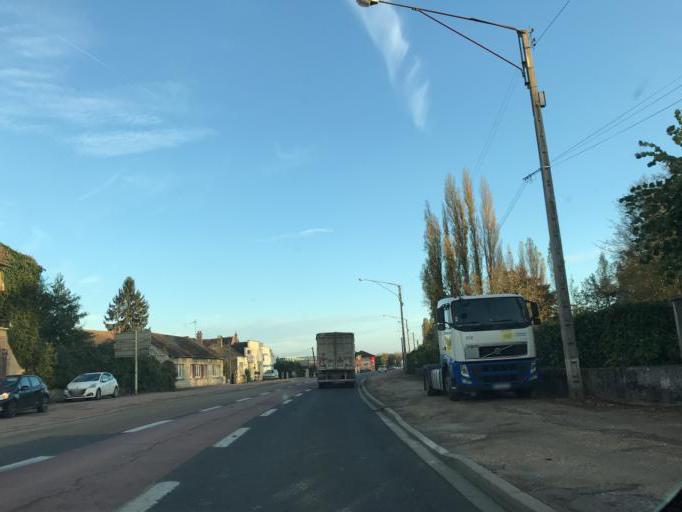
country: FR
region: Bourgogne
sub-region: Departement de l'Yonne
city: Pont-sur-Yonne
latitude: 48.2861
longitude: 3.2090
